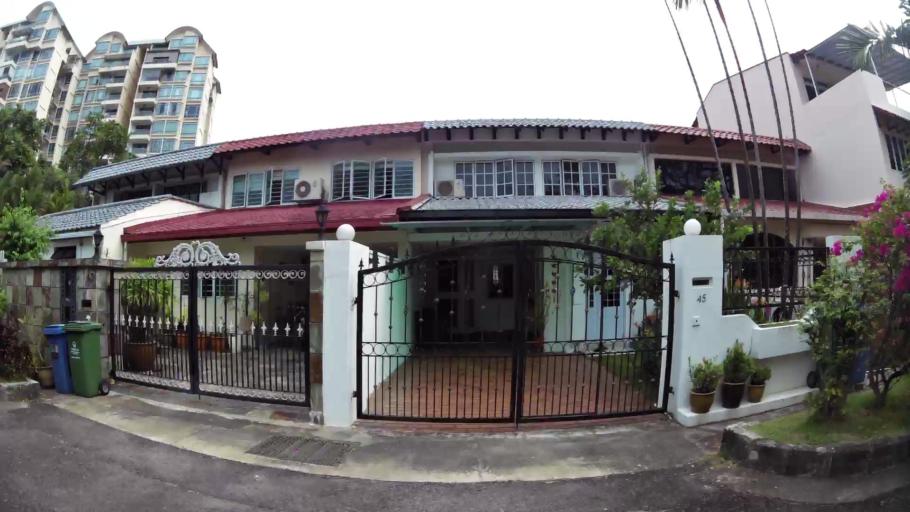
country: SG
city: Singapore
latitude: 1.3165
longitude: 103.7562
